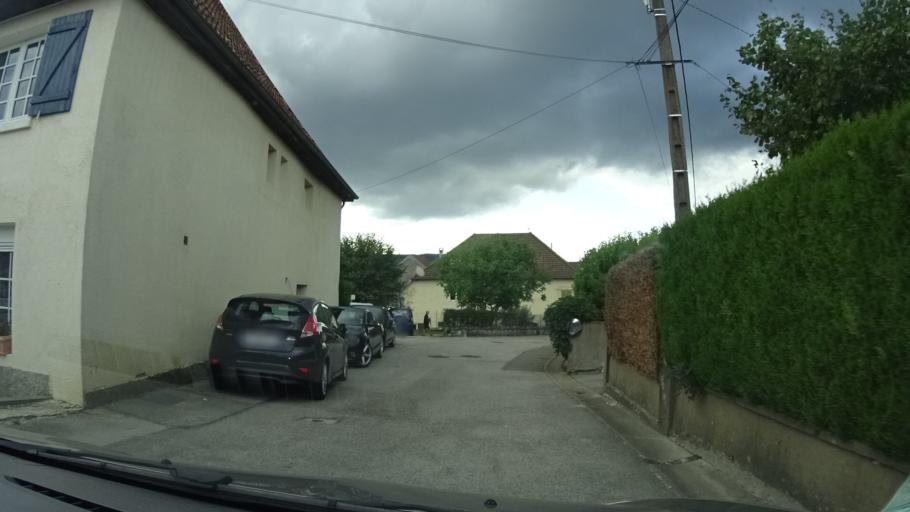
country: FR
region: Franche-Comte
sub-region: Departement du Doubs
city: Saone
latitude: 47.2190
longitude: 6.1099
